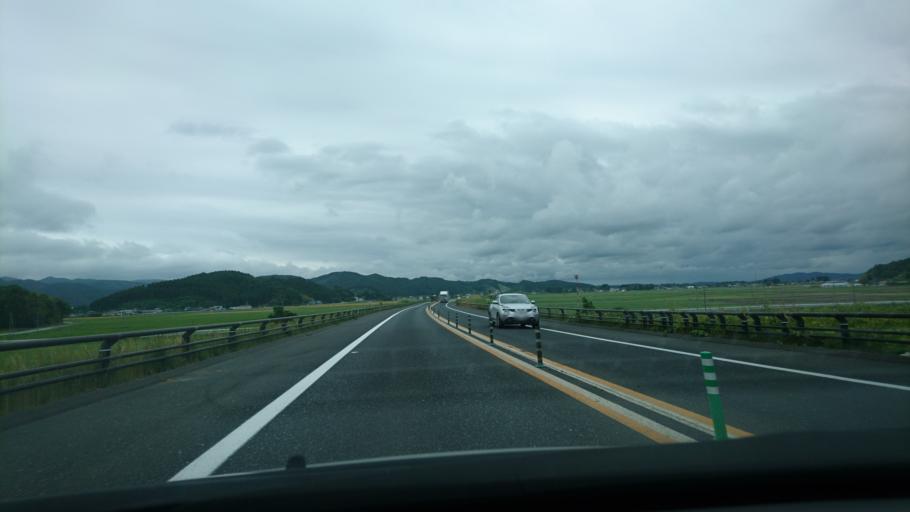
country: JP
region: Miyagi
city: Wakuya
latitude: 38.6227
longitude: 141.2855
